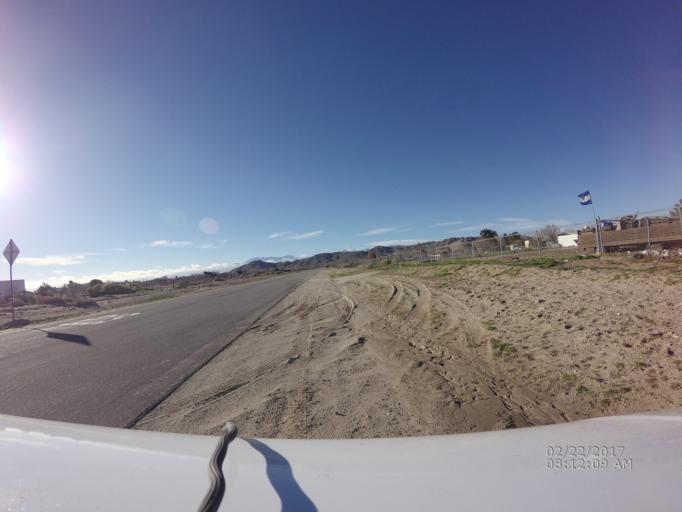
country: US
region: California
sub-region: Los Angeles County
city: Lake Los Angeles
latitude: 34.6300
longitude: -117.8449
